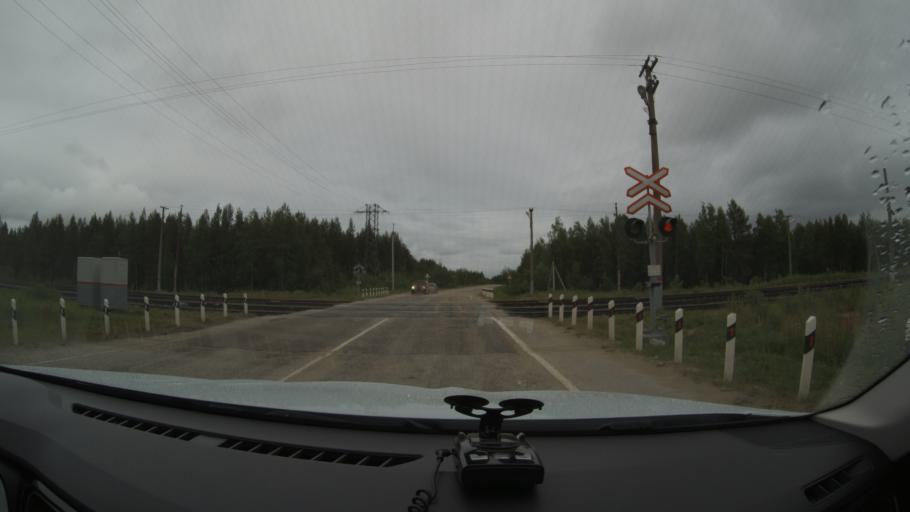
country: RU
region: Komi Republic
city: Kozhva
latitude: 65.1108
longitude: 57.0054
